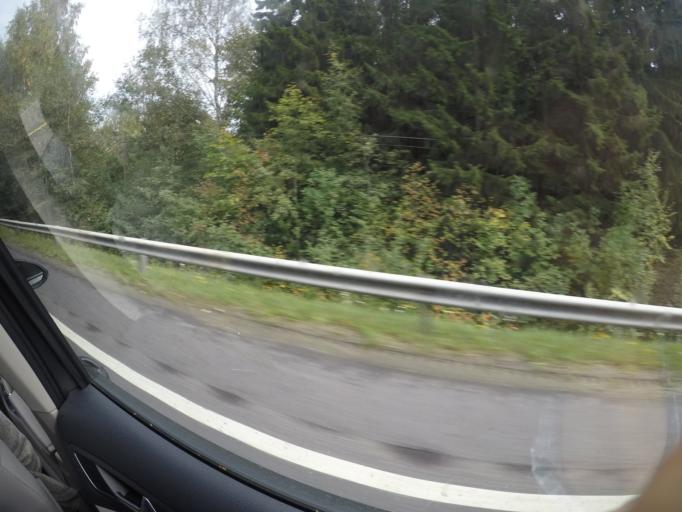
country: FI
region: Haeme
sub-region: Haemeenlinna
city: Parola
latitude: 61.0807
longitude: 24.3951
